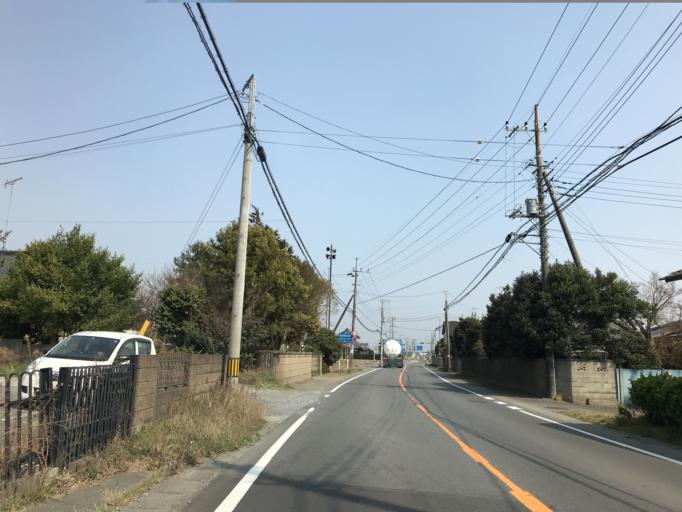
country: JP
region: Ibaraki
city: Tsukuba
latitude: 36.1483
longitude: 140.1600
